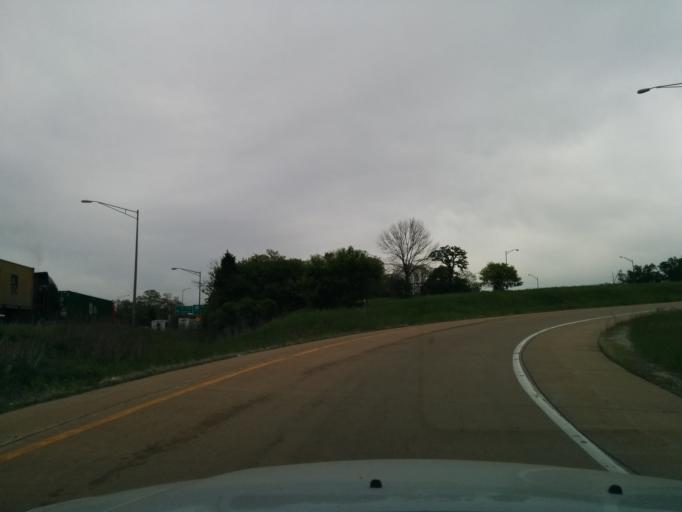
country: US
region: Illinois
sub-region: Cook County
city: Willow Springs
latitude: 41.7451
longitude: -87.8508
